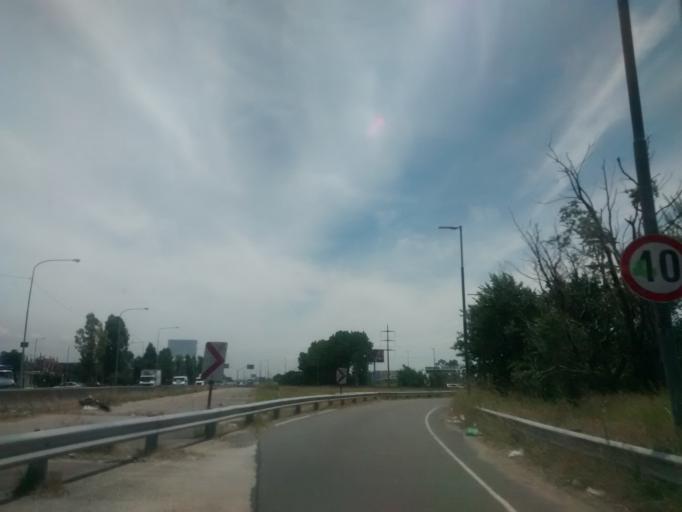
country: AR
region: Buenos Aires
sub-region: Partido de Avellaneda
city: Avellaneda
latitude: -34.6801
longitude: -58.3253
